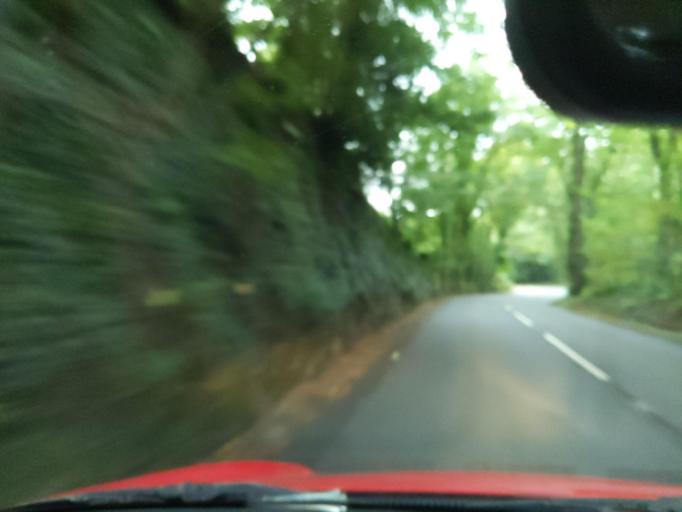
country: GB
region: England
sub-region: Devon
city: Great Torrington
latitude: 50.9415
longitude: -4.1416
